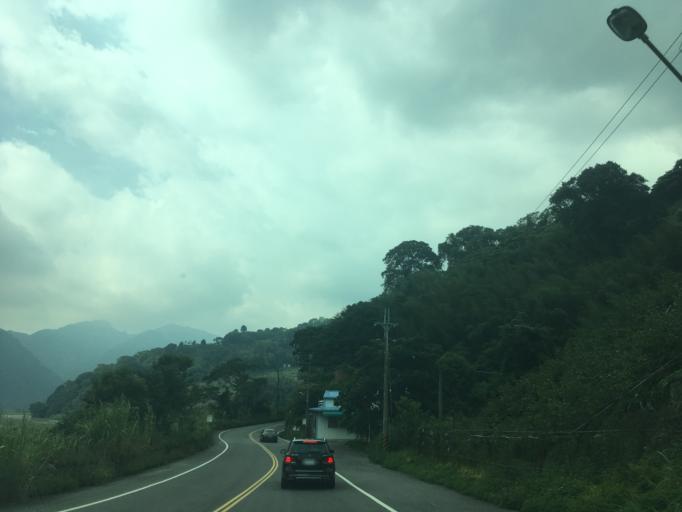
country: TW
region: Taiwan
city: Fengyuan
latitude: 24.3151
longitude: 120.9226
